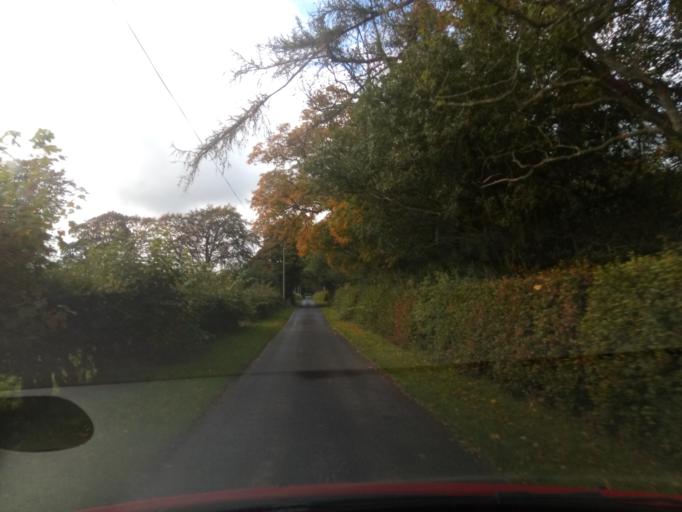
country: GB
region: Scotland
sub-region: The Scottish Borders
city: Galashiels
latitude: 55.6729
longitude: -2.8243
